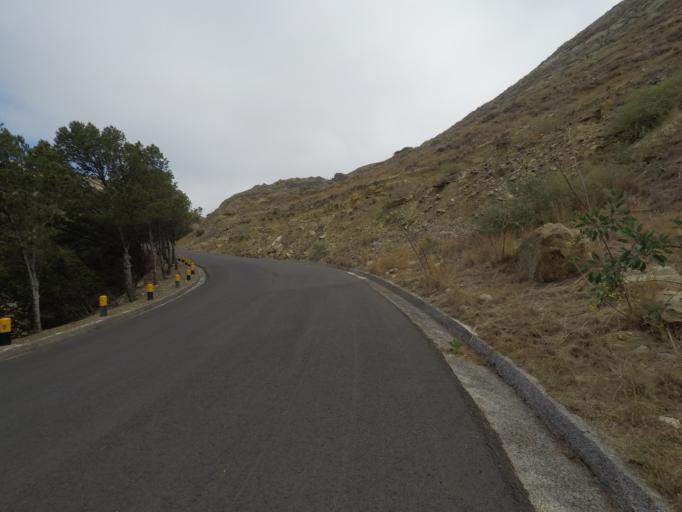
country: PT
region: Madeira
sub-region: Porto Santo
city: Camacha
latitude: 33.0930
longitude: -16.3116
